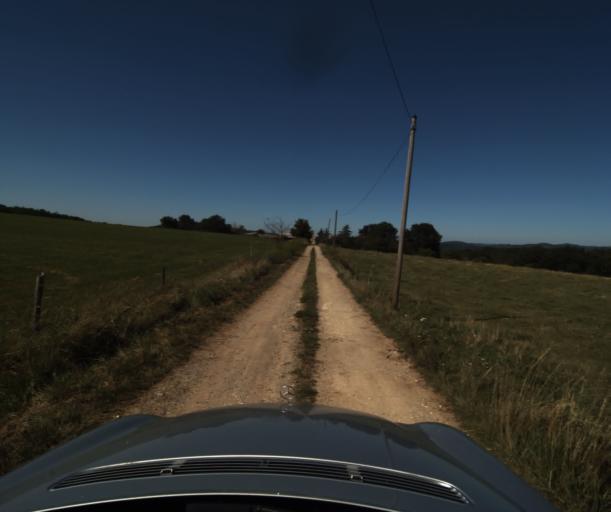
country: FR
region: Midi-Pyrenees
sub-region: Departement de l'Ariege
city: Belesta
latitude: 42.9650
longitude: 1.9099
